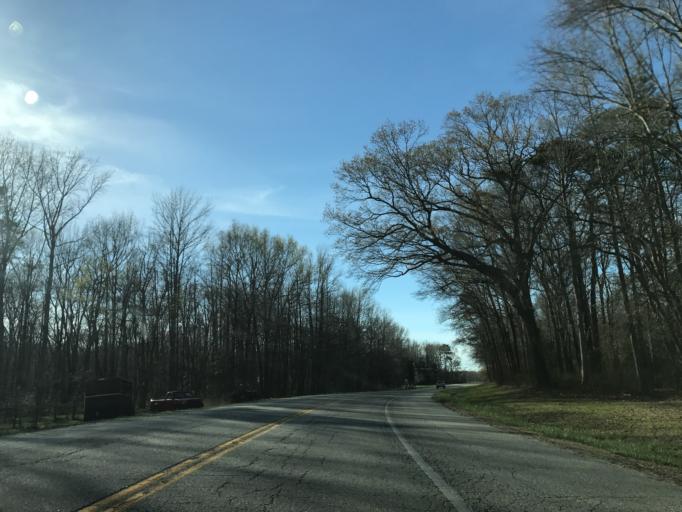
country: US
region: Maryland
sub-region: Caroline County
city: Greensboro
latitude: 39.1162
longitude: -75.7561
